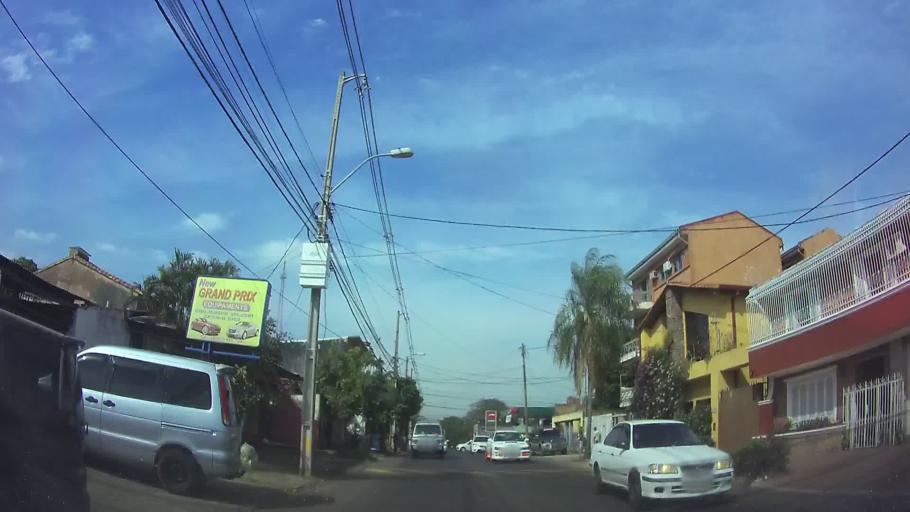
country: PY
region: Asuncion
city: Asuncion
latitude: -25.3020
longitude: -57.6102
